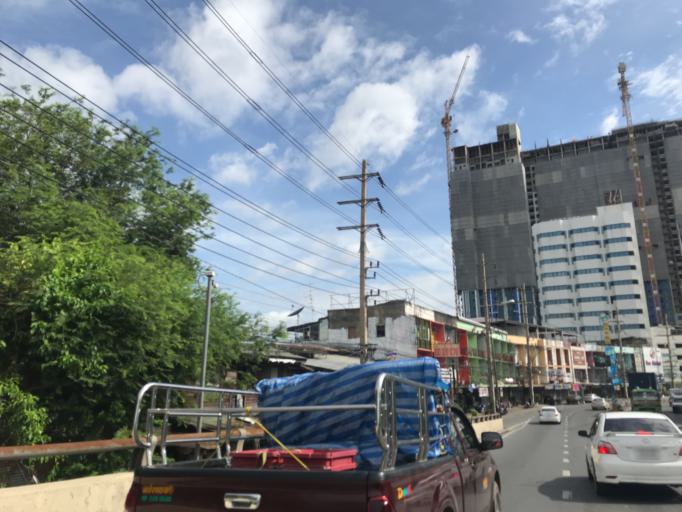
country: TH
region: Bangkok
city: Watthana
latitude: 13.7386
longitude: 100.5986
